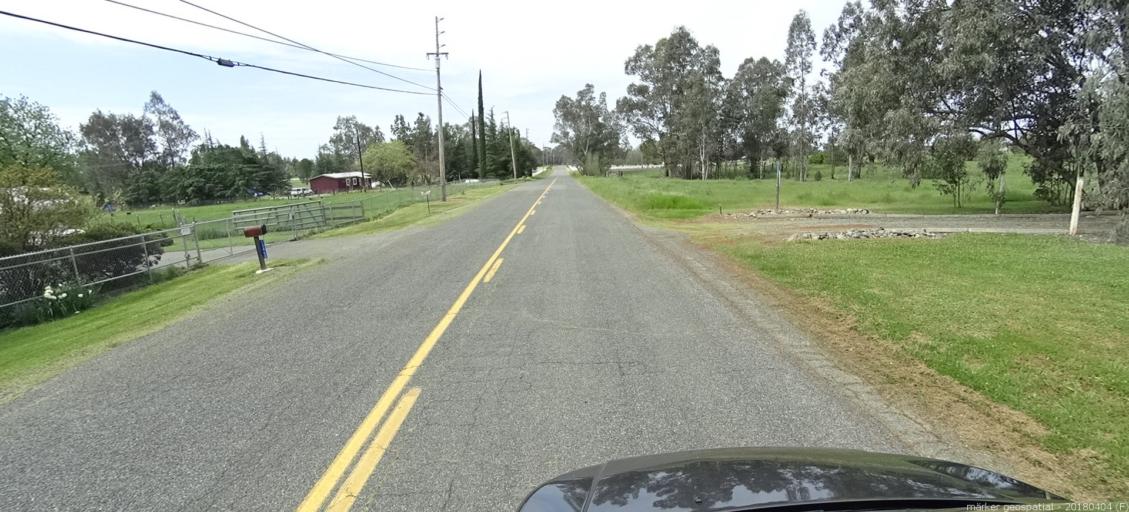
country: US
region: California
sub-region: Sacramento County
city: Clay
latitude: 38.3141
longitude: -121.1635
